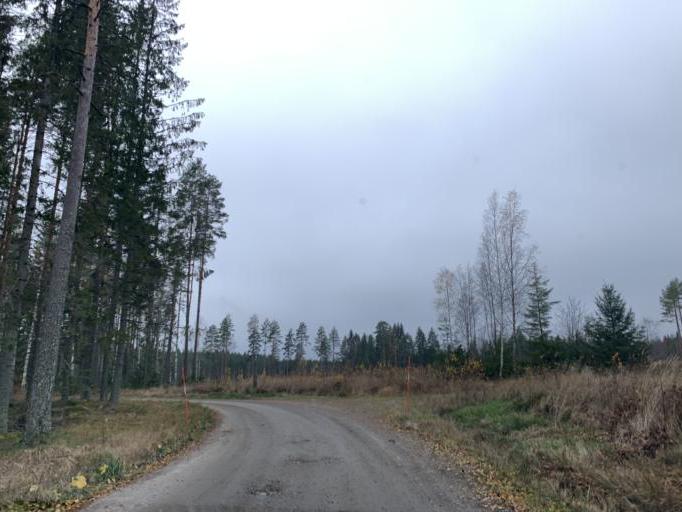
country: SE
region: Vaestmanland
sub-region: Surahammars Kommun
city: Ramnas
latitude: 59.7377
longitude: 16.1196
